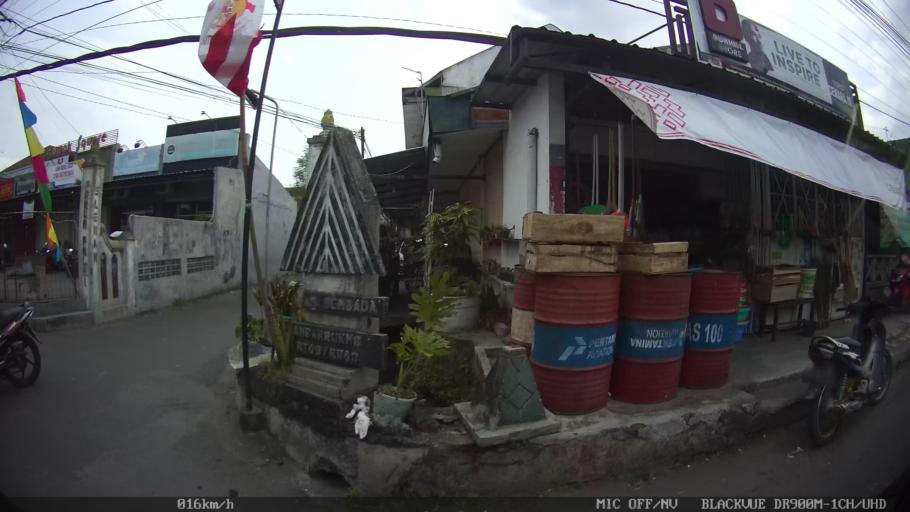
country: ID
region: Daerah Istimewa Yogyakarta
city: Depok
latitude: -7.7846
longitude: 110.3997
